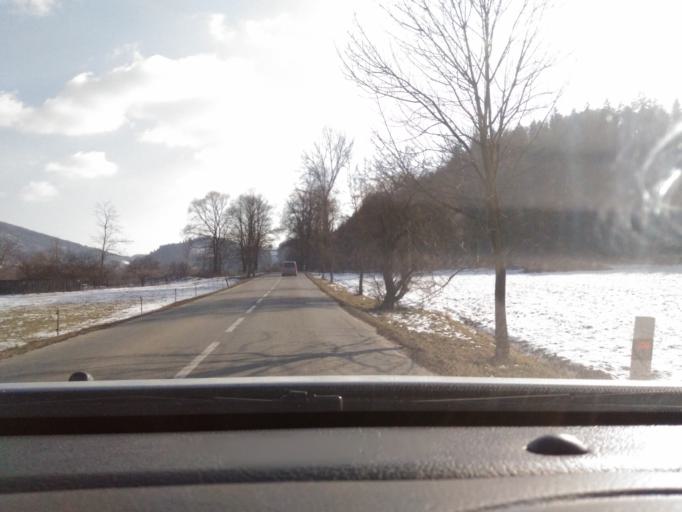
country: CZ
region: South Moravian
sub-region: Okres Brno-Venkov
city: Nedvedice
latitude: 49.4376
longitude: 16.3438
